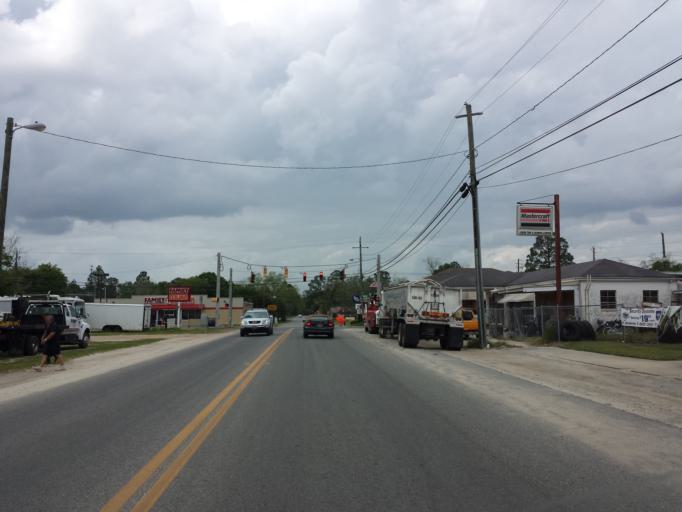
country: US
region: Georgia
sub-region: Cook County
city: Sparks
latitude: 31.2711
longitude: -83.4650
